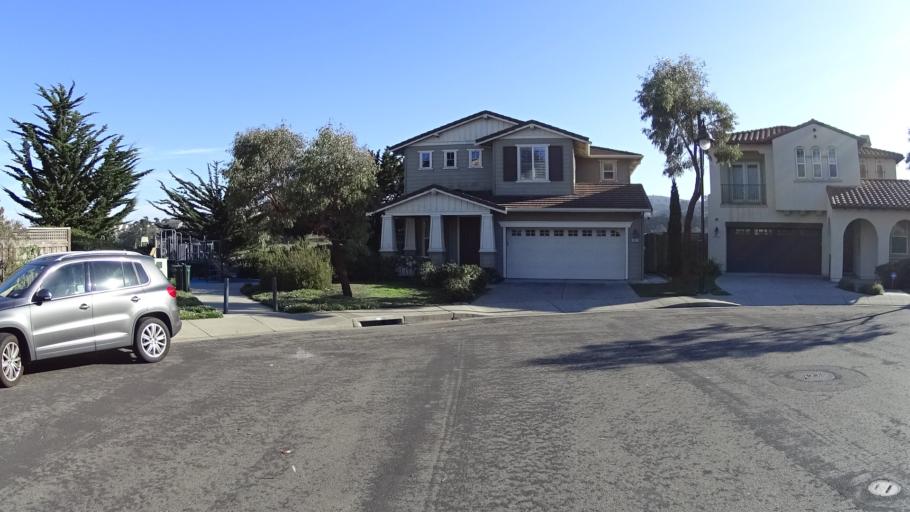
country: US
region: California
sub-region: San Mateo County
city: Pacifica
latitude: 37.6329
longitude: -122.4639
